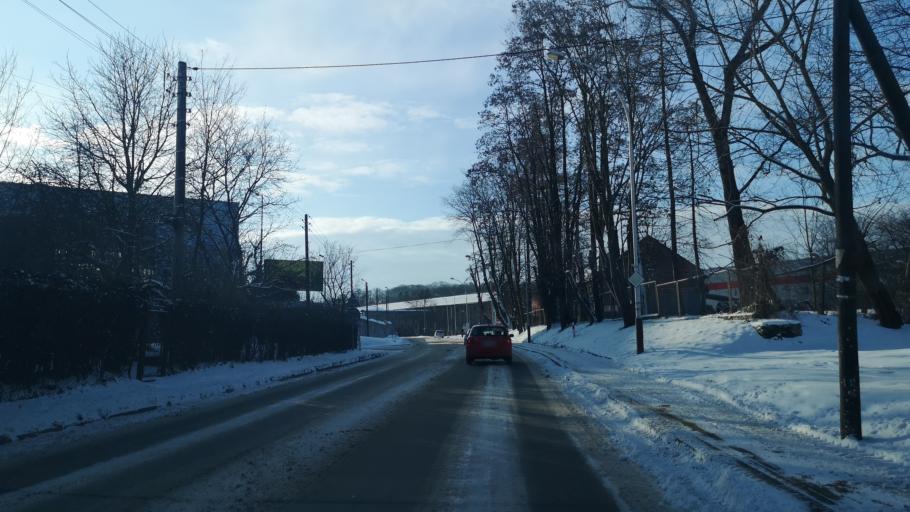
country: PL
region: Subcarpathian Voivodeship
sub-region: Powiat przeworski
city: Przeworsk
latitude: 50.0678
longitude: 22.4905
